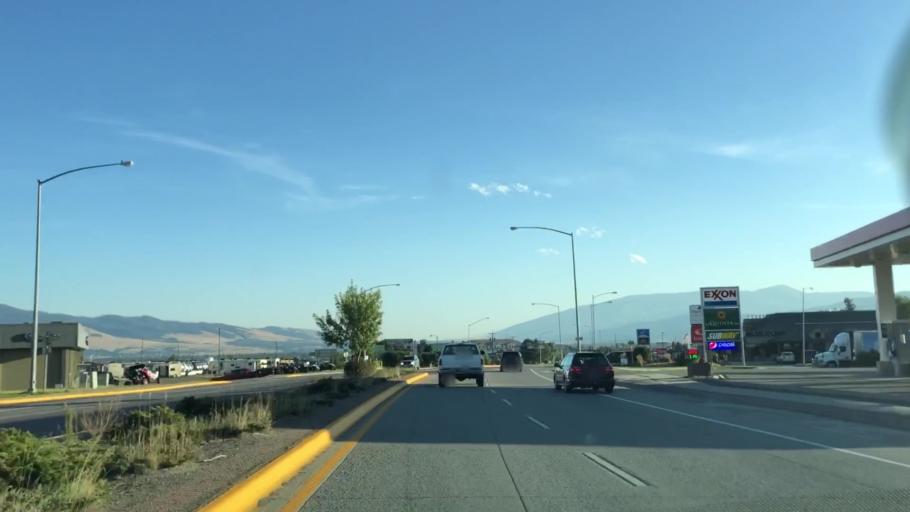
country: US
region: Montana
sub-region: Missoula County
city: Orchard Homes
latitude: 46.9123
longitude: -114.0347
